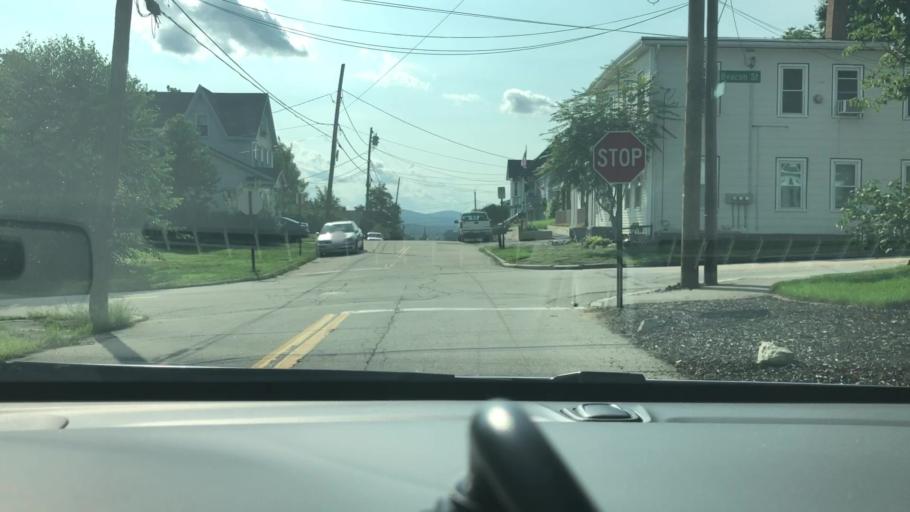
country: US
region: New Hampshire
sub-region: Hillsborough County
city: Manchester
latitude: 42.9894
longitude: -71.4428
